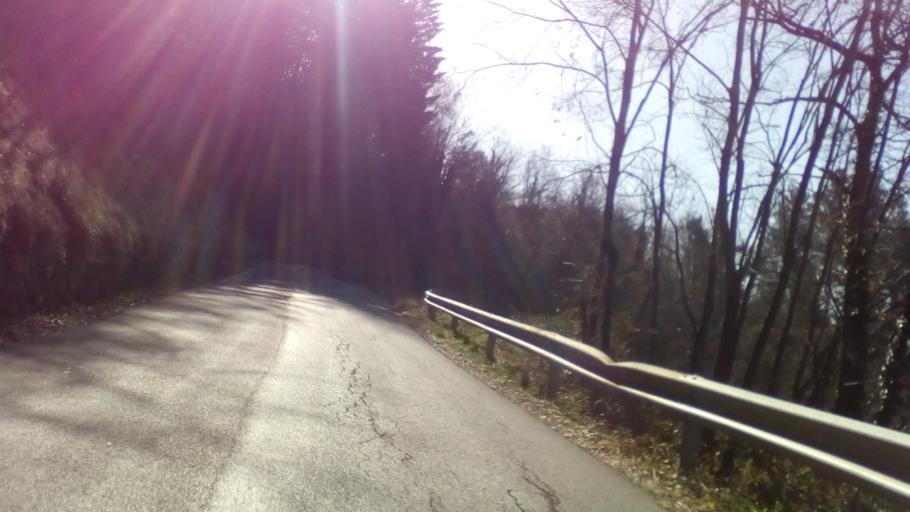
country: IT
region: Tuscany
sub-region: Provincia di Lucca
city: Castiglione di Garfagnana
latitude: 44.1438
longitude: 10.4300
